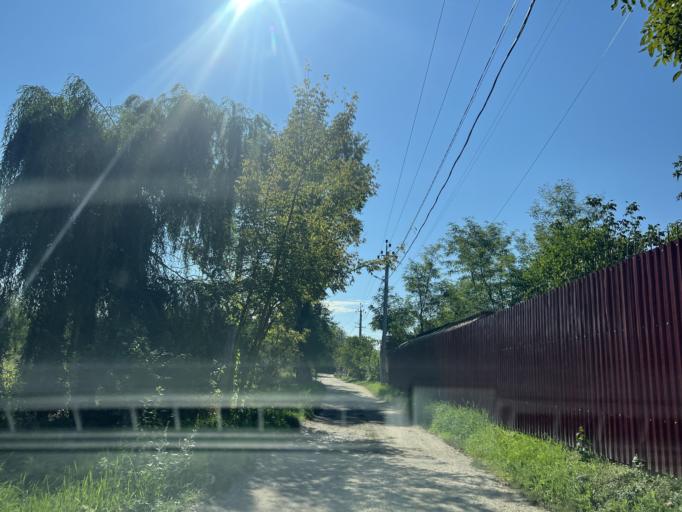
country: RO
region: Iasi
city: Ungheni-Prut
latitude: 47.1990
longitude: 27.7900
